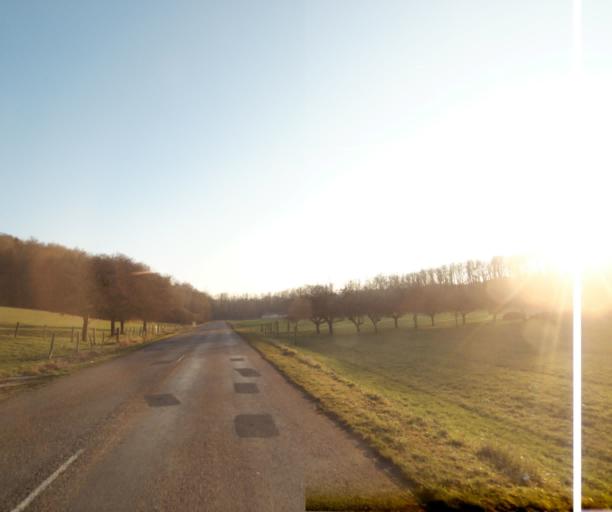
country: FR
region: Champagne-Ardenne
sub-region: Departement de la Haute-Marne
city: Chevillon
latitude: 48.5352
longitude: 5.1062
